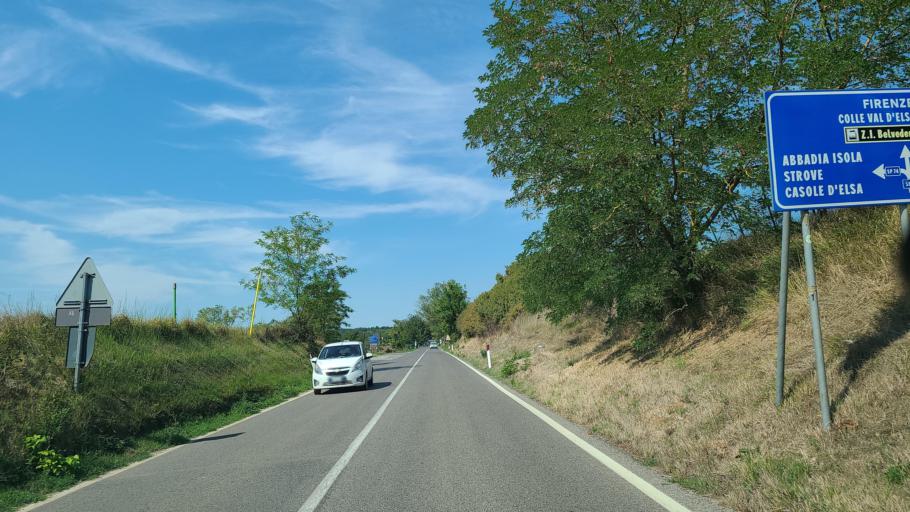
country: IT
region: Tuscany
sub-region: Provincia di Siena
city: Castellina Scalo
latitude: 43.3930
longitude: 11.2015
